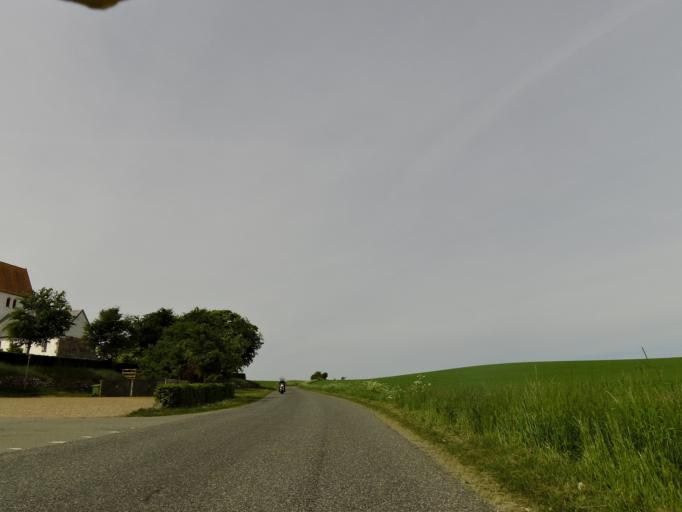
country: DK
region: Central Jutland
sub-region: Holstebro Kommune
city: Vinderup
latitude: 56.5790
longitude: 8.8483
